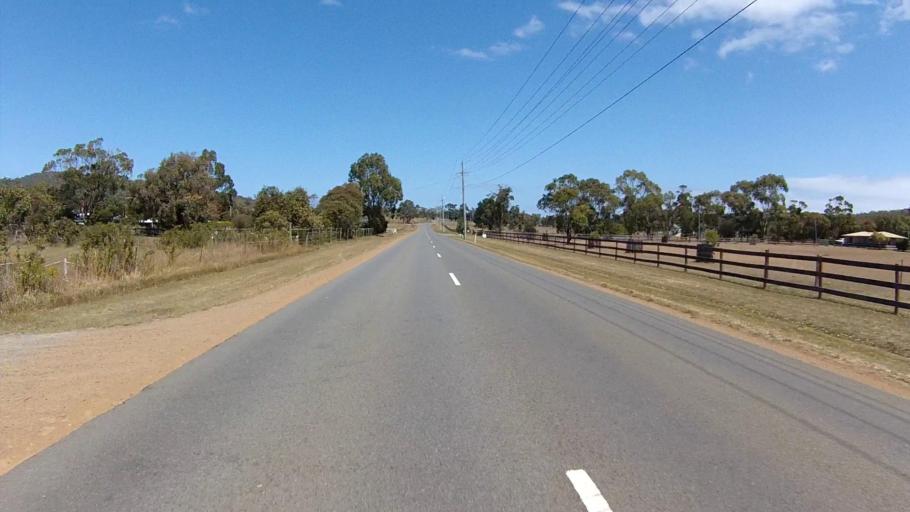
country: AU
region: Tasmania
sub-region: Clarence
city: Sandford
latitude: -42.9486
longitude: 147.4816
